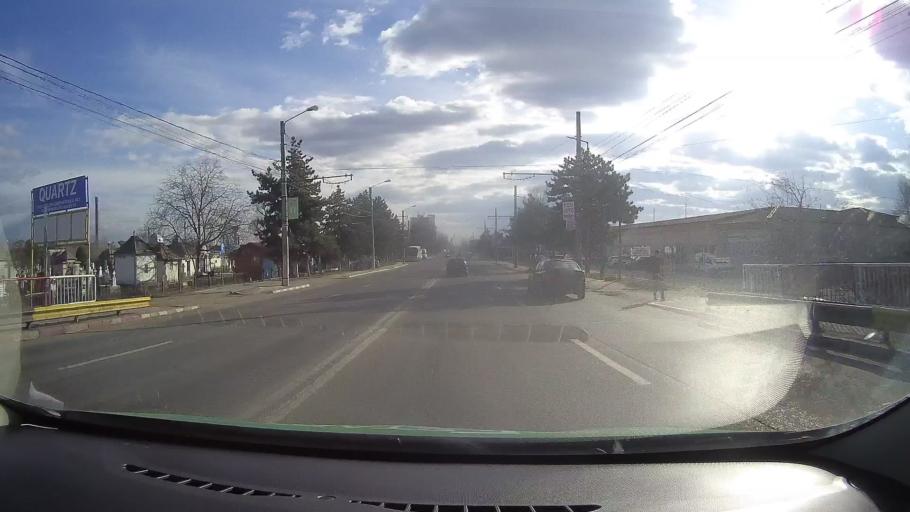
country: RO
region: Dambovita
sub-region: Comuna Lucieni
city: Lucieni
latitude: 44.8533
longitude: 25.4286
